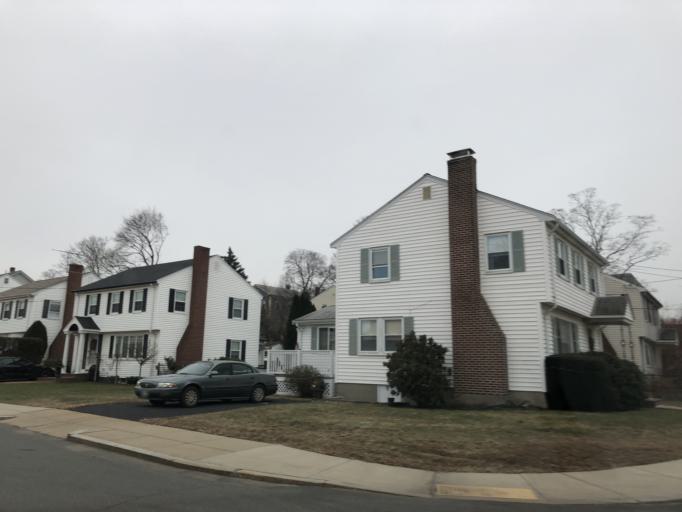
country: US
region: Massachusetts
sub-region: Middlesex County
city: Watertown
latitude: 42.3540
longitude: -71.1519
